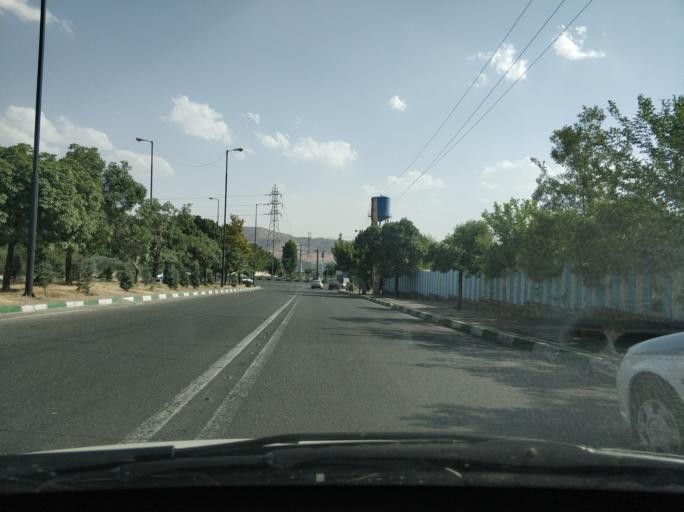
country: IR
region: Tehran
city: Tajrish
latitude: 35.7460
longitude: 51.5767
